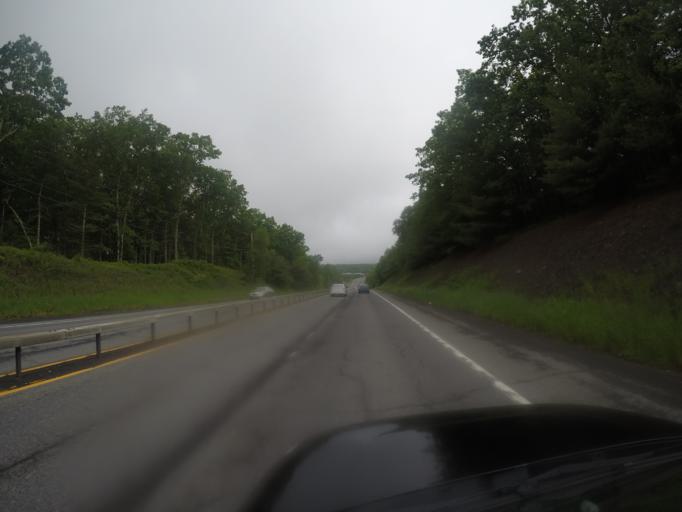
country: US
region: New York
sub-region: Ulster County
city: West Hurley
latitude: 41.9752
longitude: -74.0825
